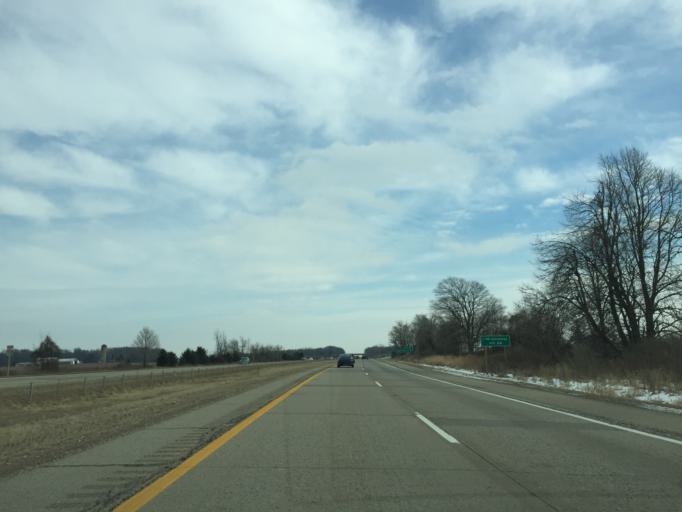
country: US
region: Michigan
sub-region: Ionia County
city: Saranac
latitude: 42.8792
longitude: -85.1443
